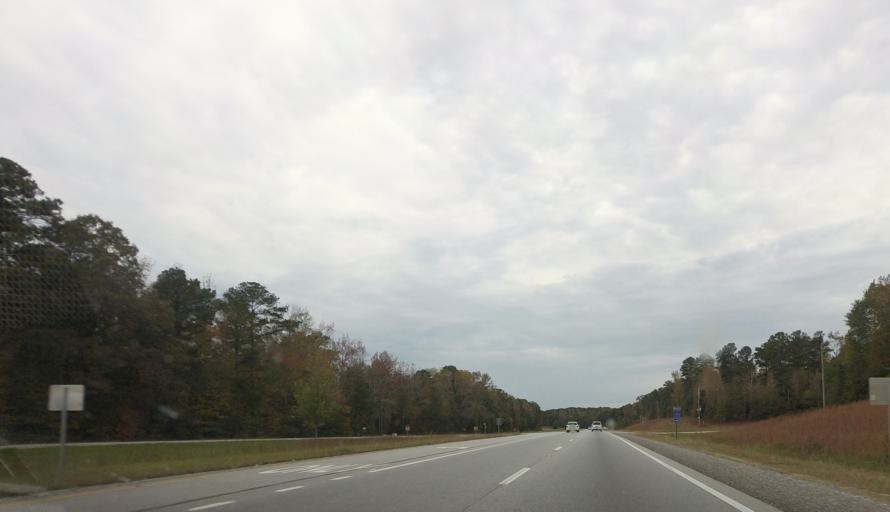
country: US
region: Alabama
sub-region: Lee County
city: Opelika
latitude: 32.6298
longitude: -85.2826
